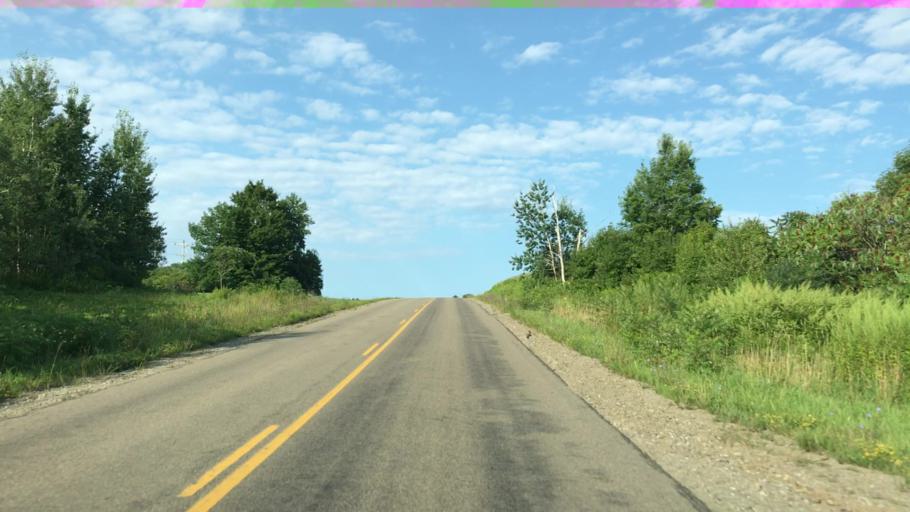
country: US
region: New York
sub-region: Chautauqua County
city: Brocton
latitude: 42.3126
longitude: -79.3693
